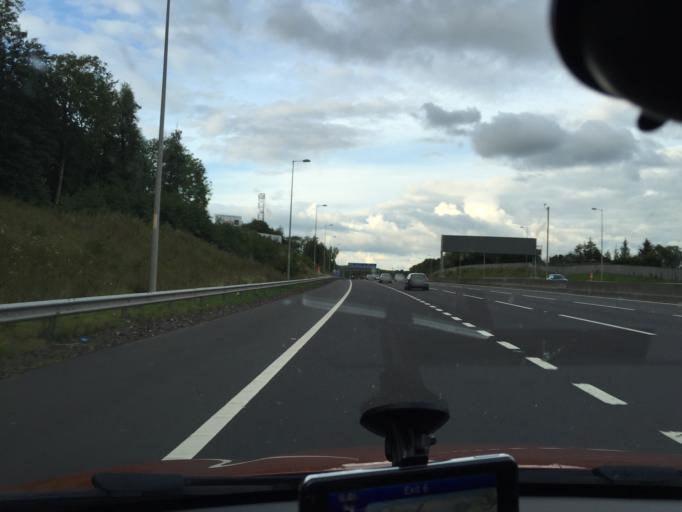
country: GB
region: Scotland
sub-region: North Lanarkshire
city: Glenboig
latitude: 55.9269
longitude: -4.0442
